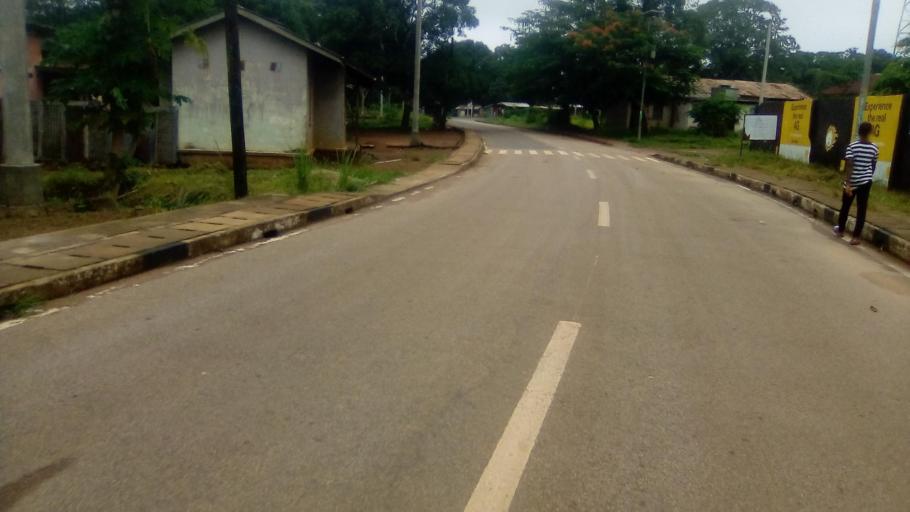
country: SL
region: Southern Province
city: Moyamba
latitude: 8.1617
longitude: -12.4359
